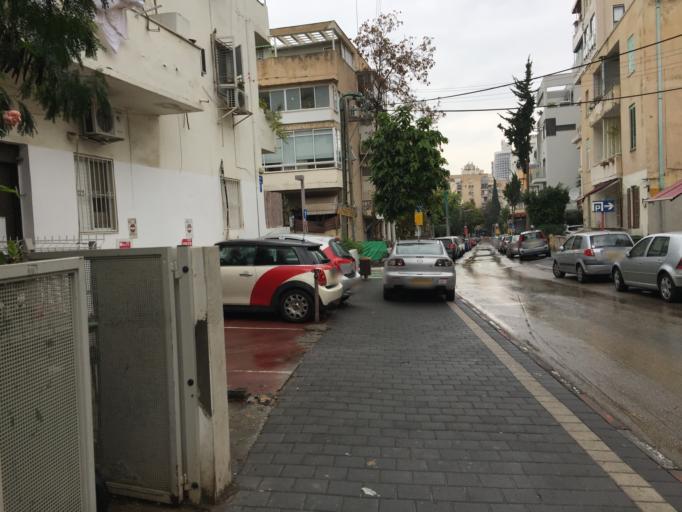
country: IL
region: Tel Aviv
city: Tel Aviv
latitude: 32.0684
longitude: 34.7730
